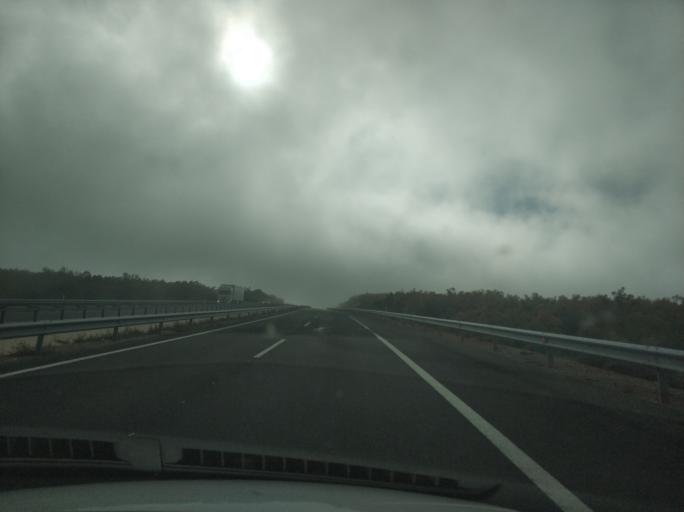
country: ES
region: Castille and Leon
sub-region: Provincia de Soria
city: Adradas
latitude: 41.3111
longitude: -2.4823
